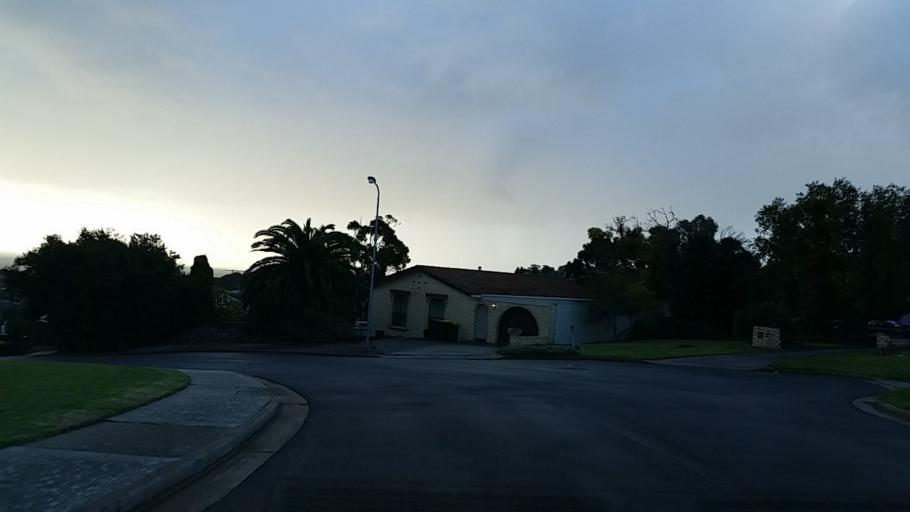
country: AU
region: South Australia
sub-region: Marion
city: Happy Valley
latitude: -35.0742
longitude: 138.5086
